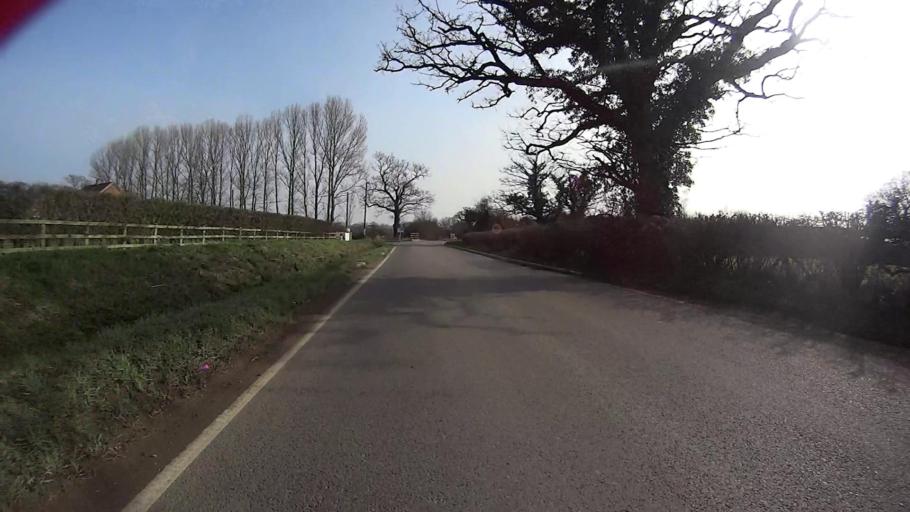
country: GB
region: England
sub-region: Surrey
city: Felbridge
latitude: 51.1830
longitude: -0.0684
